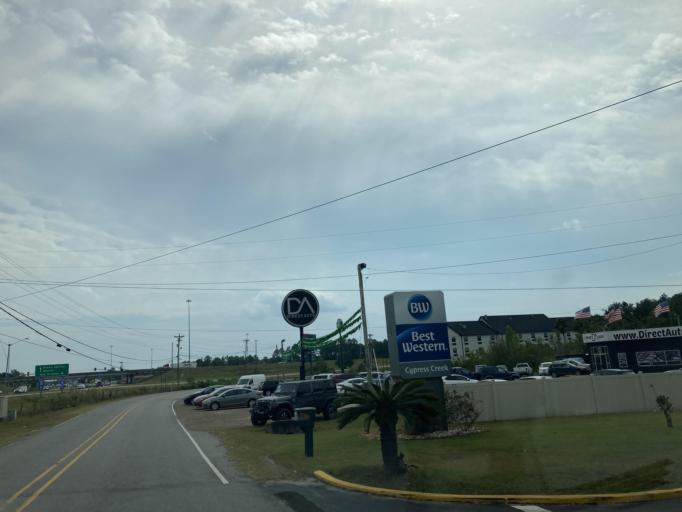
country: US
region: Mississippi
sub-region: Jackson County
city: Gulf Hills
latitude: 30.4575
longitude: -88.8438
